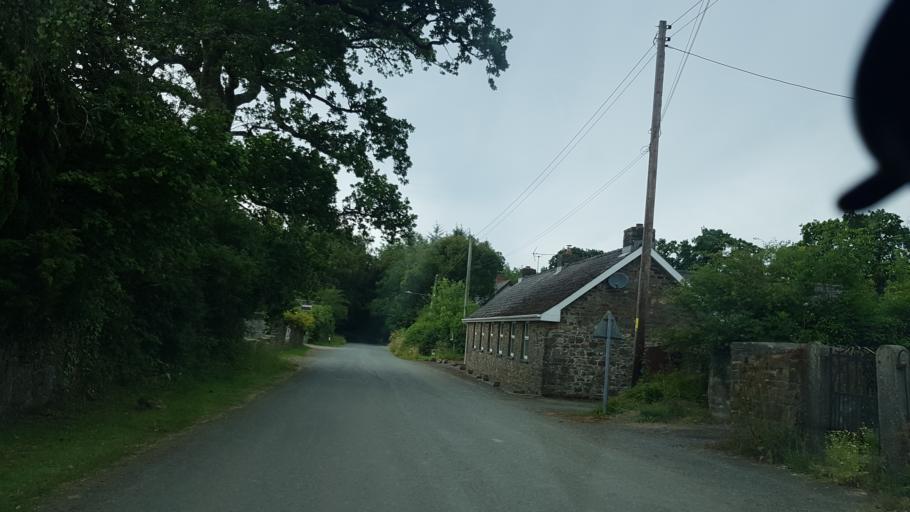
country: GB
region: Wales
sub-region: Pembrokeshire
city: Wiston
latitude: 51.7923
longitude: -4.8911
